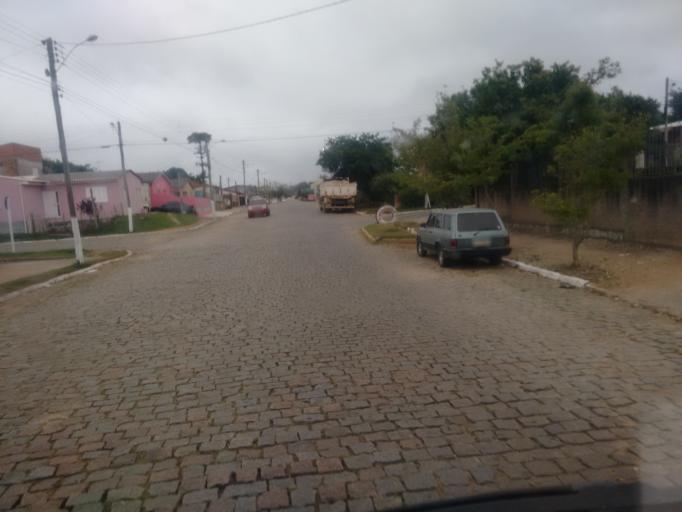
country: BR
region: Rio Grande do Sul
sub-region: Camaqua
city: Camaqua
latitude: -30.8431
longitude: -51.8150
